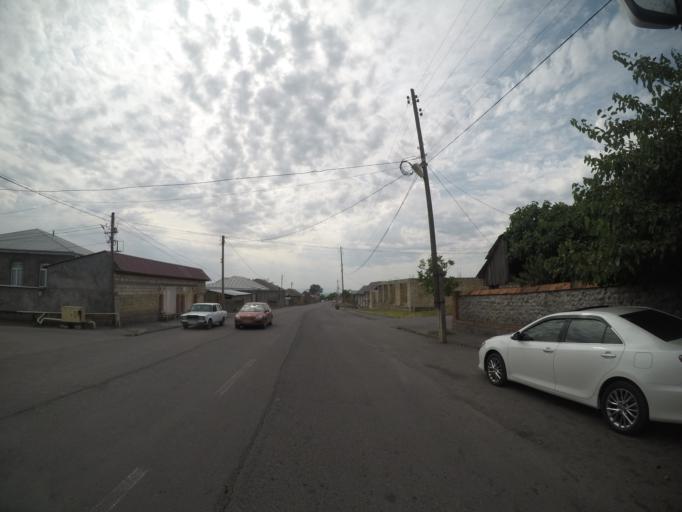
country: AZ
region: Qakh Rayon
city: Qax
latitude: 41.4146
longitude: 46.9114
